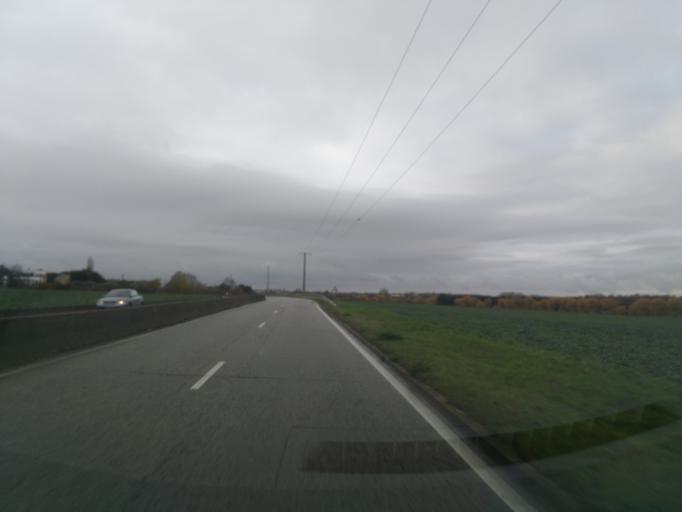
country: FR
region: Ile-de-France
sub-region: Departement des Yvelines
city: Bois-d'Arcy
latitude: 48.8202
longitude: 2.0184
